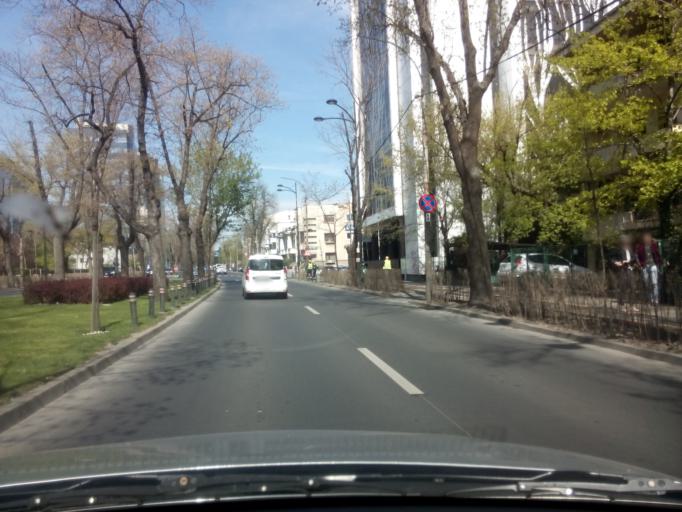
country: RO
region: Bucuresti
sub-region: Municipiul Bucuresti
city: Bucharest
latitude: 44.4636
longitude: 26.0913
